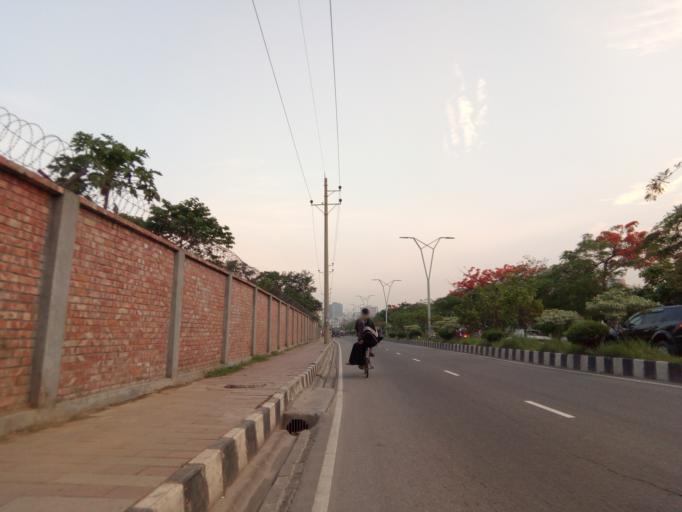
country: BD
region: Dhaka
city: Paltan
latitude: 23.7575
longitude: 90.4056
